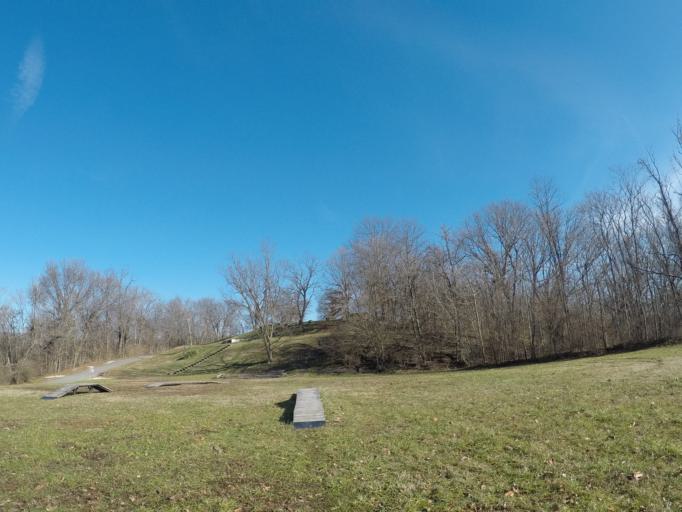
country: US
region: West Virginia
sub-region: Cabell County
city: Huntington
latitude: 38.4168
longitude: -82.3984
